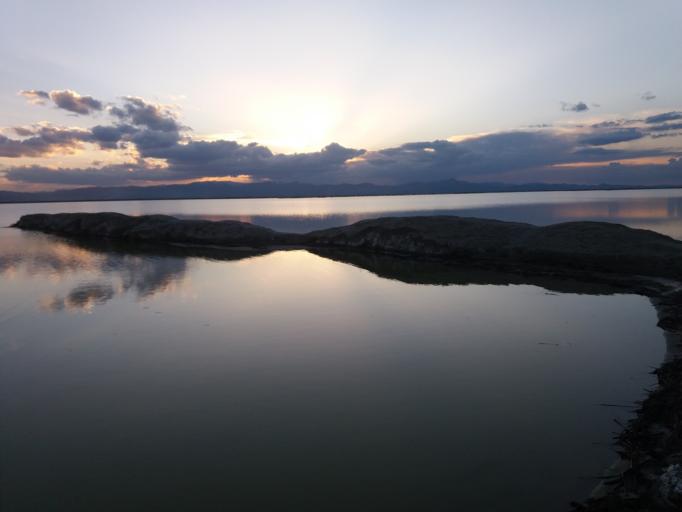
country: IR
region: Markazi
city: Arak
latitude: 34.1849
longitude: 49.8463
